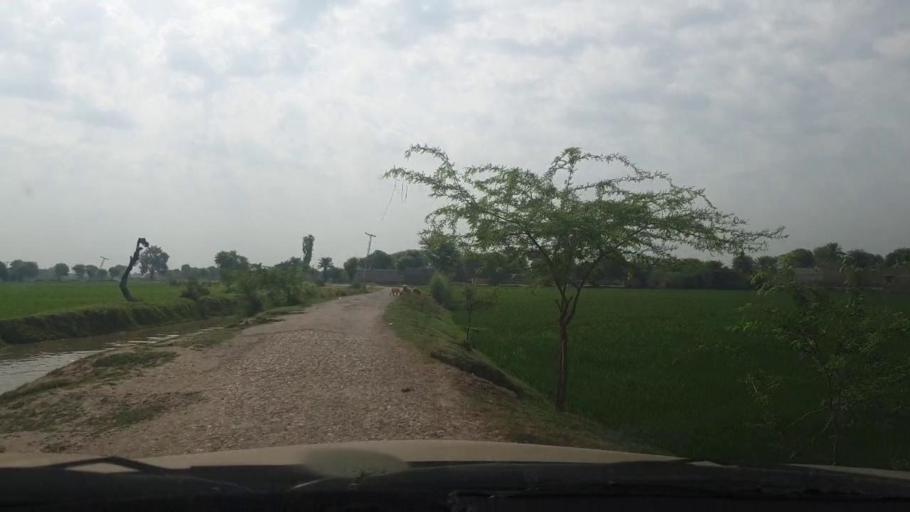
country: PK
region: Sindh
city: Larkana
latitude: 27.6391
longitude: 68.2051
